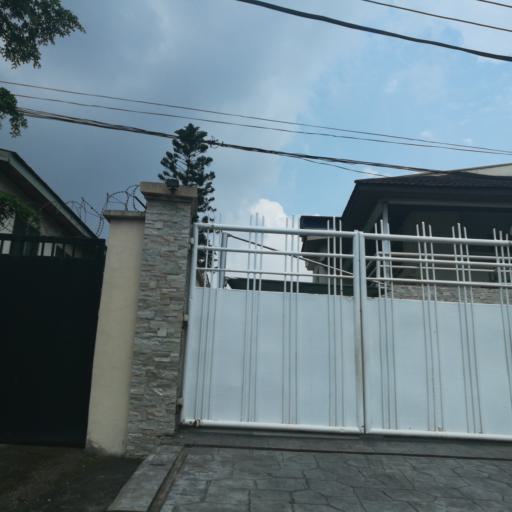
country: NG
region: Lagos
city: Ojota
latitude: 6.5749
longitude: 3.3911
